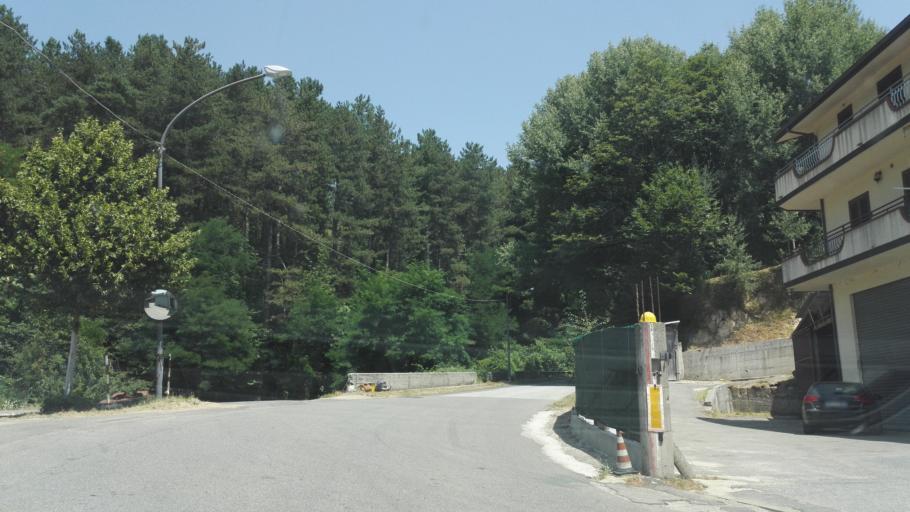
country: IT
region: Calabria
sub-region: Provincia di Vibo-Valentia
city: Mongiana
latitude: 38.5176
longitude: 16.3208
